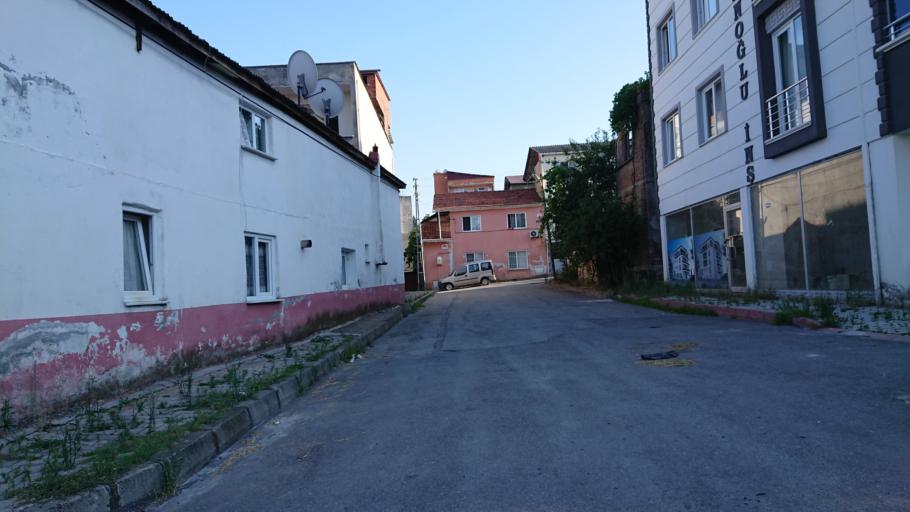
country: TR
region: Samsun
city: Samsun
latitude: 41.2986
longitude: 36.3208
